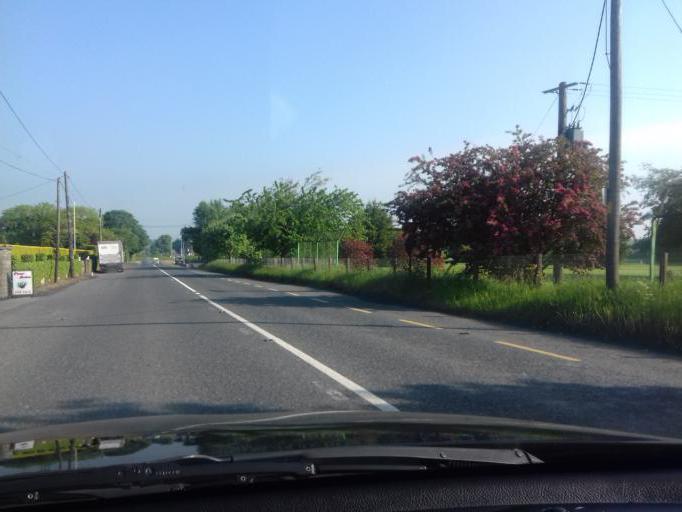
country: IE
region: Leinster
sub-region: Dublin City
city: Finglas
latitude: 53.4315
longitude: -6.3320
